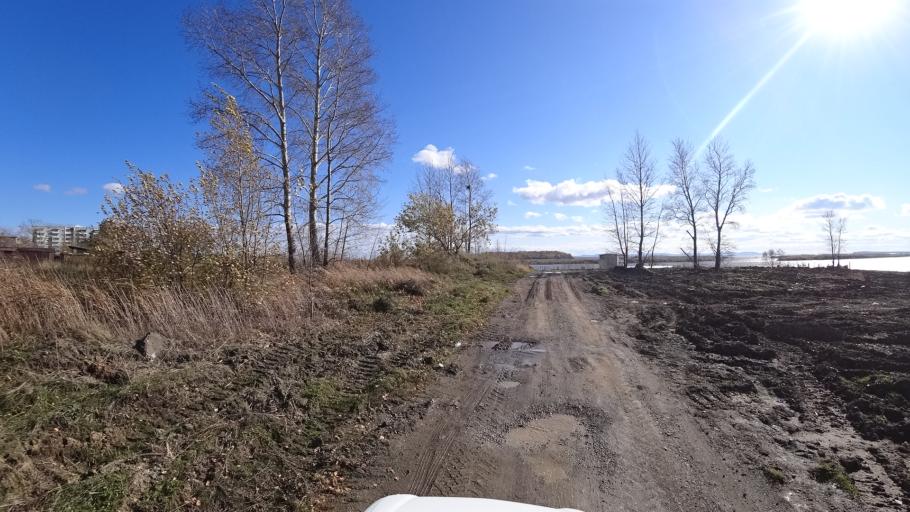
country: RU
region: Khabarovsk Krai
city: Amursk
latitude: 50.2154
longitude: 136.8889
